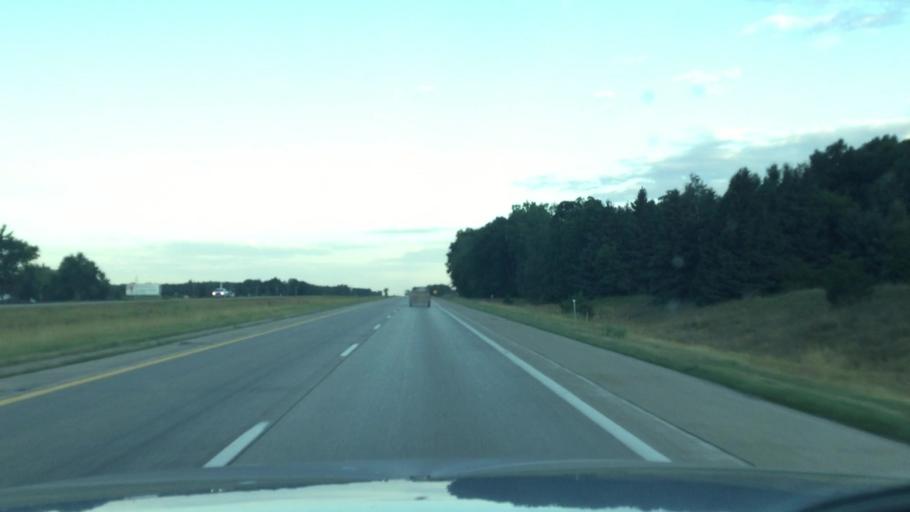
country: US
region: Michigan
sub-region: Shiawassee County
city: Perry
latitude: 42.8113
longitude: -84.3038
